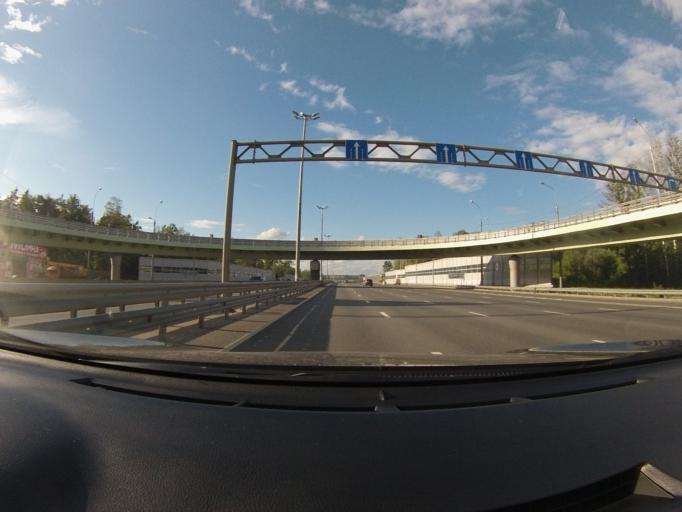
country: RU
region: Moskovskaya
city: Bolshevo
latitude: 55.9405
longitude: 37.8128
